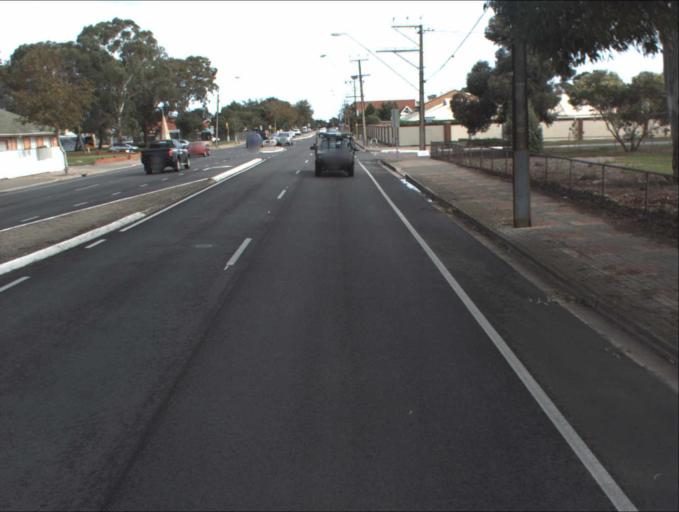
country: AU
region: South Australia
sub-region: Port Adelaide Enfield
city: Klemzig
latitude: -34.8717
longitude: 138.6253
